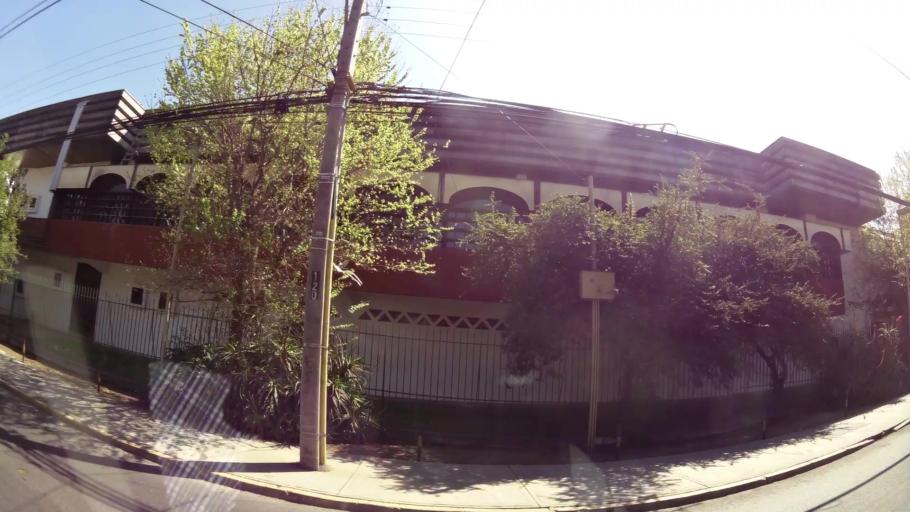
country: CL
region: Santiago Metropolitan
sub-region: Provincia de Santiago
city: Villa Presidente Frei, Nunoa, Santiago, Chile
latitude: -33.4156
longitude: -70.5754
